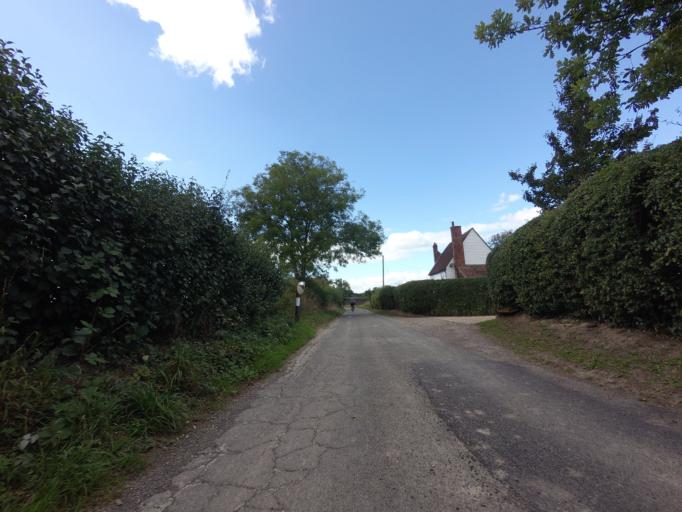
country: GB
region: England
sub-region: Kent
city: Marden
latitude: 51.1508
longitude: 0.4881
